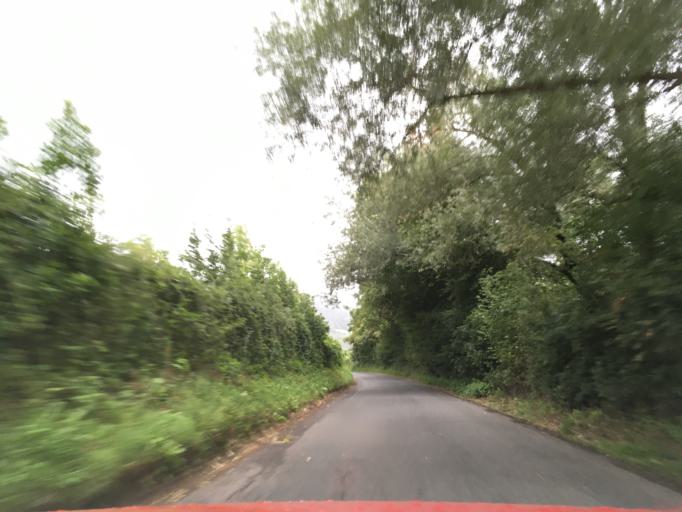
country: GB
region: Wales
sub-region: Monmouthshire
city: Llangybi
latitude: 51.6536
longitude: -2.8849
